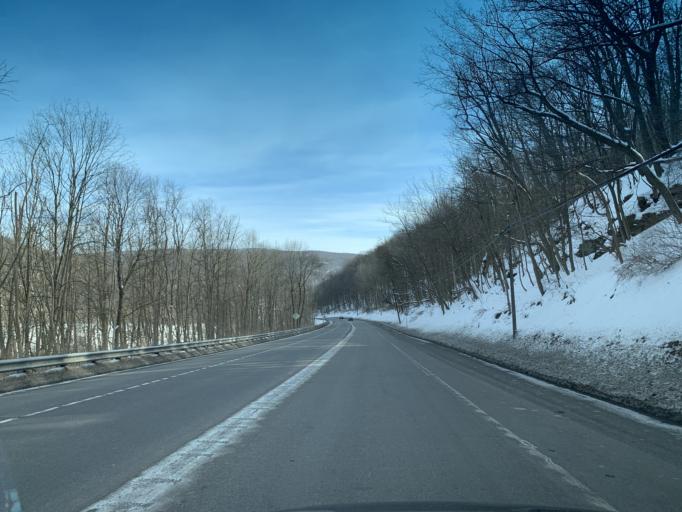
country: US
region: Maryland
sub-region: Allegany County
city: Frostburg
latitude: 39.6488
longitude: -78.8937
